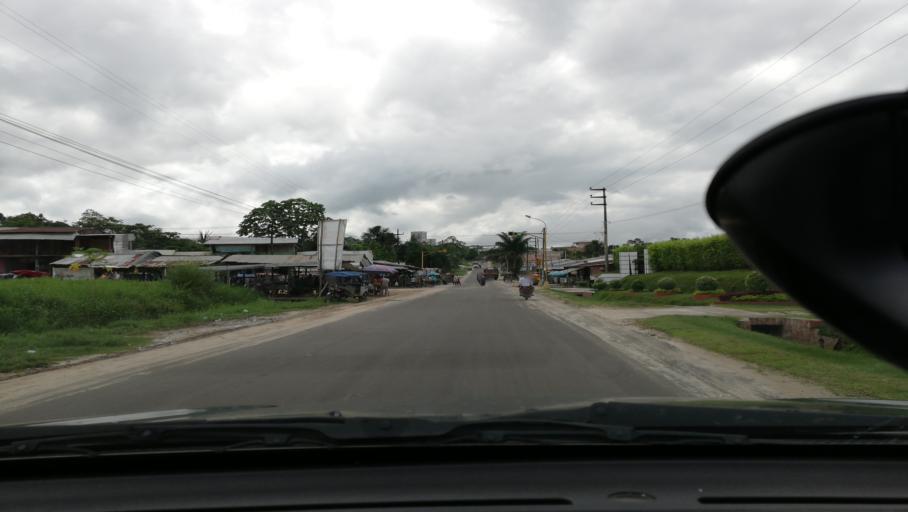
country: PE
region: Loreto
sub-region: Provincia de Maynas
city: Iquitos
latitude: -3.8469
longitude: -73.3371
